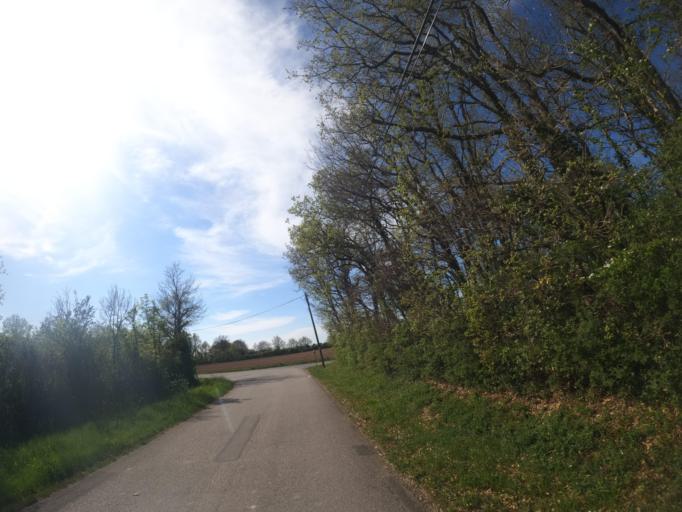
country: FR
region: Poitou-Charentes
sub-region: Departement des Deux-Sevres
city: Saint-Jean-de-Thouars
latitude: 46.9273
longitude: -0.2176
